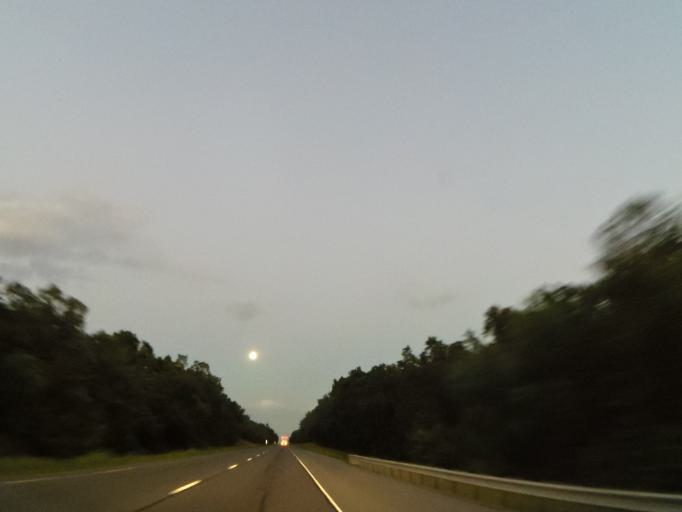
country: US
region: Tennessee
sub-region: Cumberland County
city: Crossville
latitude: 36.0374
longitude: -85.1058
